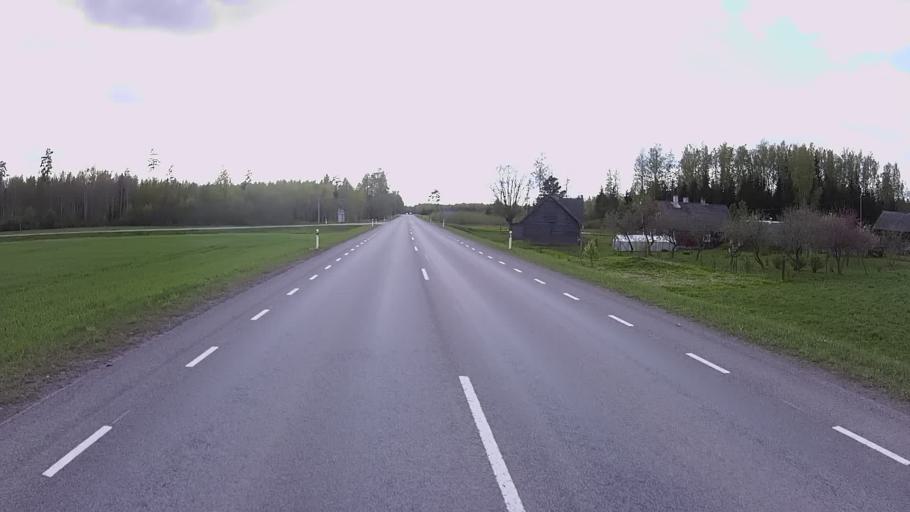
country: EE
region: Tartu
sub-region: Alatskivi vald
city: Kallaste
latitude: 58.5141
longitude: 26.9746
